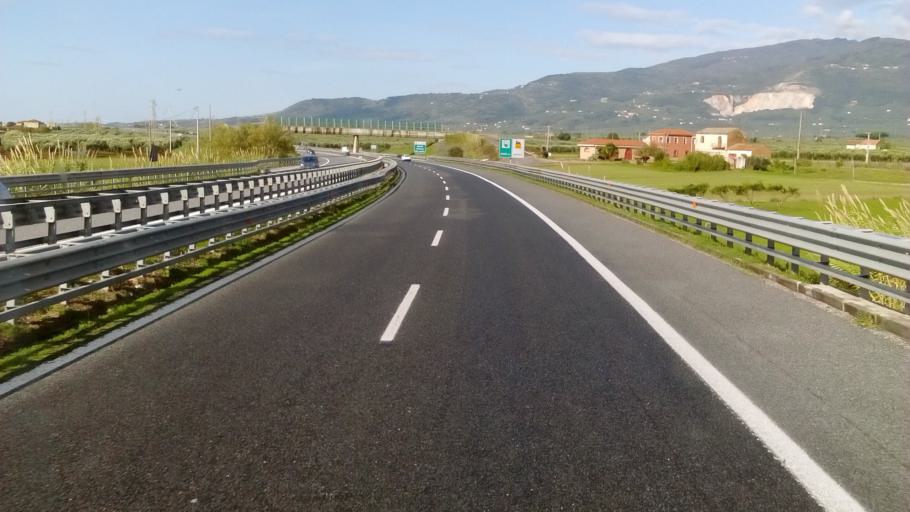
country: IT
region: Calabria
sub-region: Provincia di Catanzaro
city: Santa Eufemia Lamezia
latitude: 38.9215
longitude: 16.2621
